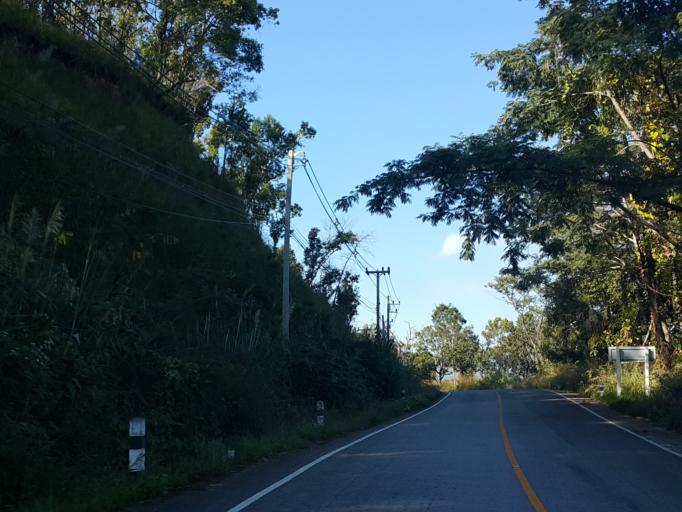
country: TH
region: Chiang Mai
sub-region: Amphoe Chiang Dao
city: Chiang Dao
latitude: 19.5279
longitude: 98.8755
